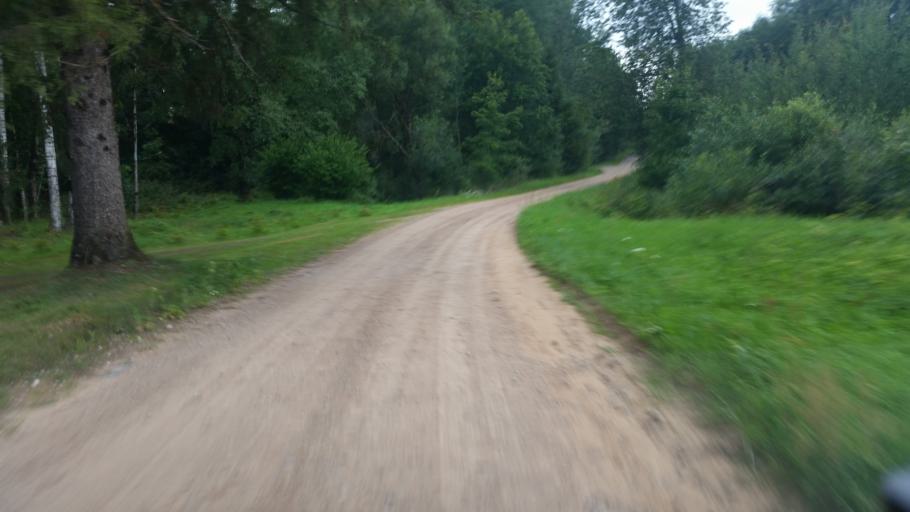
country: LV
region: Vecumnieki
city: Vecumnieki
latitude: 56.4403
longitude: 24.6253
